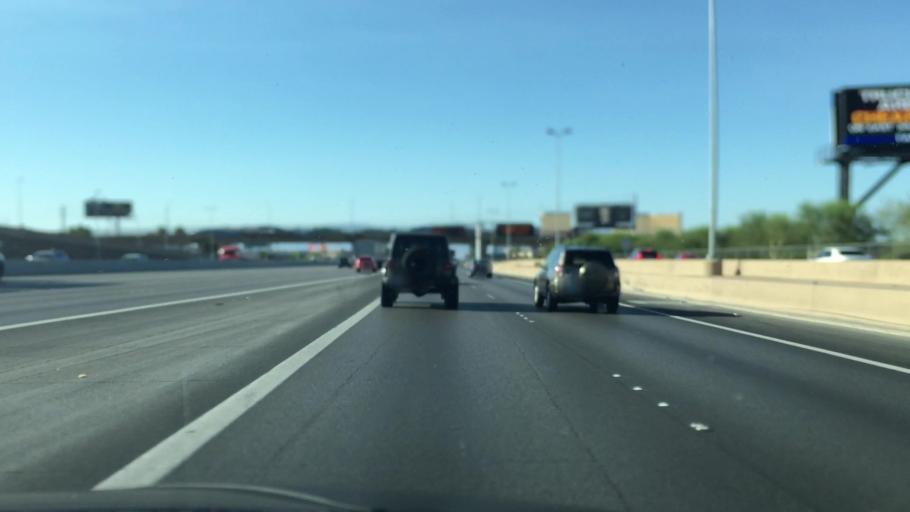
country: US
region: Nevada
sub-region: Clark County
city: Paradise
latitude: 36.0686
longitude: -115.1805
